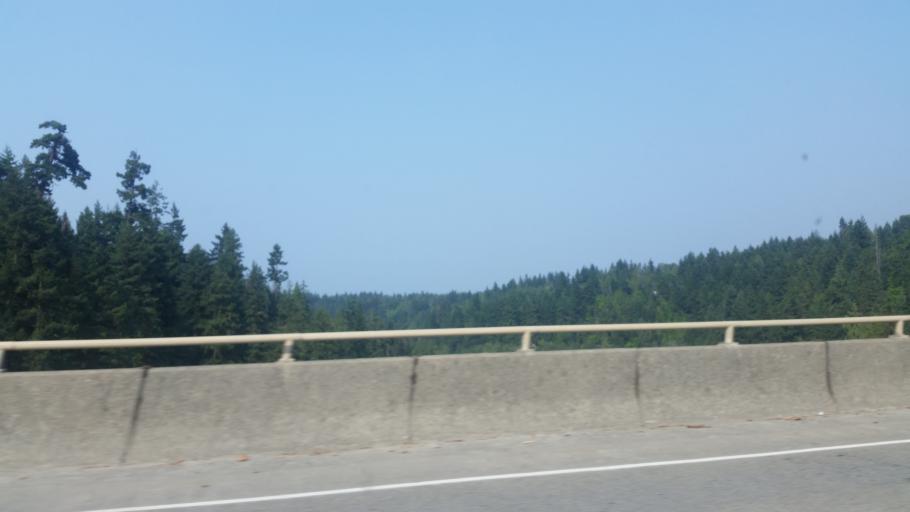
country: US
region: Washington
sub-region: Clallam County
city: Port Angeles
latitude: 48.1011
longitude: -123.5578
